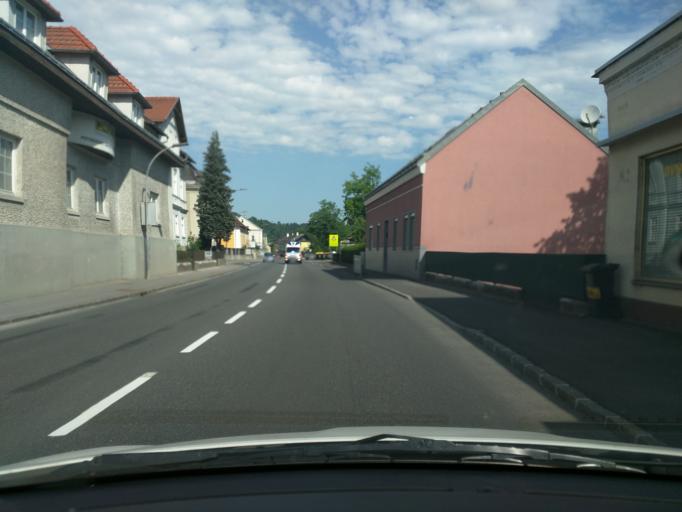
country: AT
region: Lower Austria
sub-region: Waidhofen an der Ybbs Stadt
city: Waidhofen an der Ybbs
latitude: 47.9689
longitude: 14.7661
